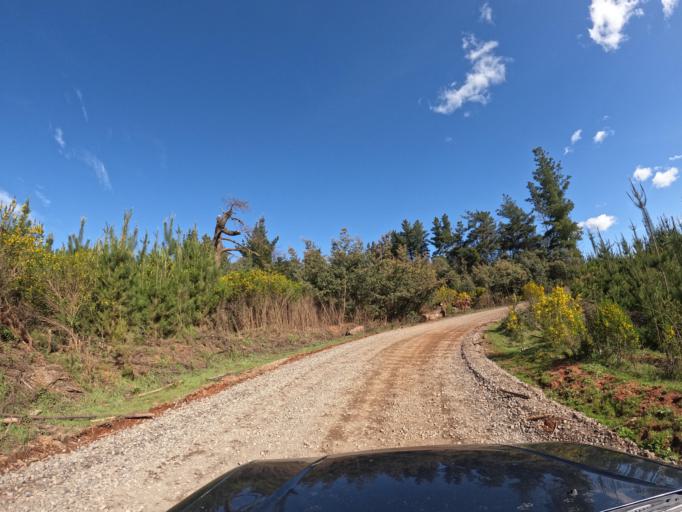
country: CL
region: Biobio
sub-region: Provincia de Biobio
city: La Laja
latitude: -37.0886
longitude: -72.8283
